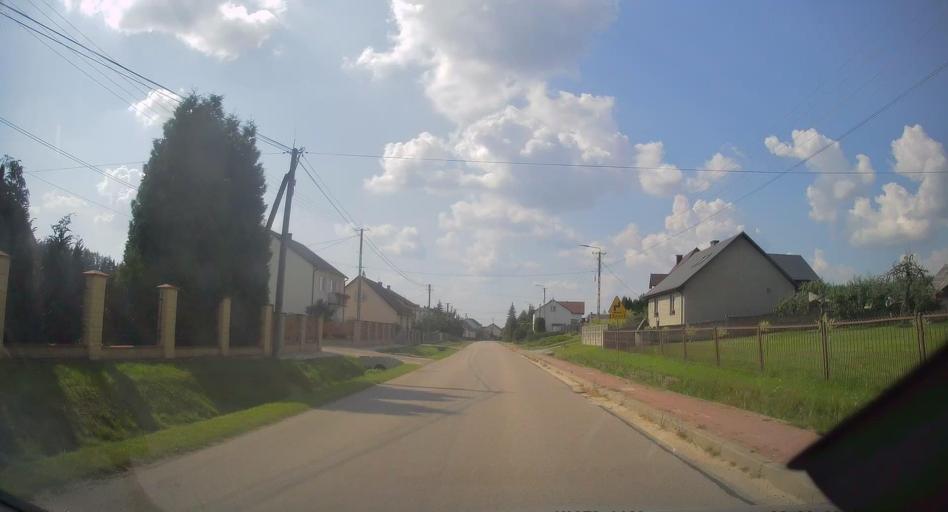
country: PL
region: Swietokrzyskie
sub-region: Powiat kielecki
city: Checiny
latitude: 50.8156
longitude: 20.4041
